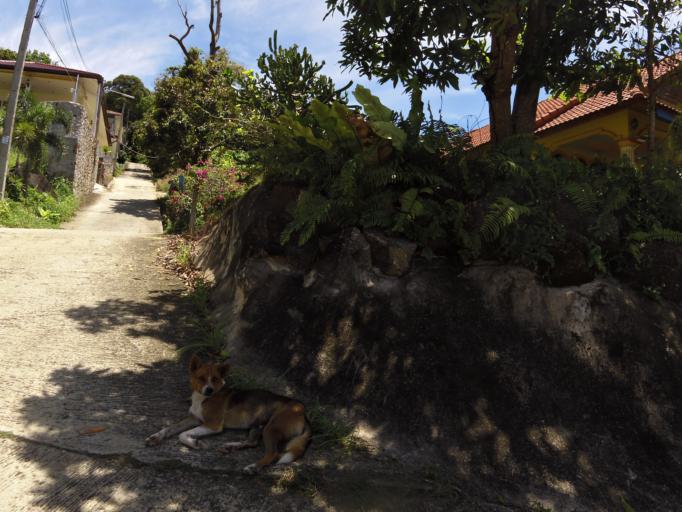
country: TH
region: Phuket
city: Ban Karon
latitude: 7.8509
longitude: 98.3056
